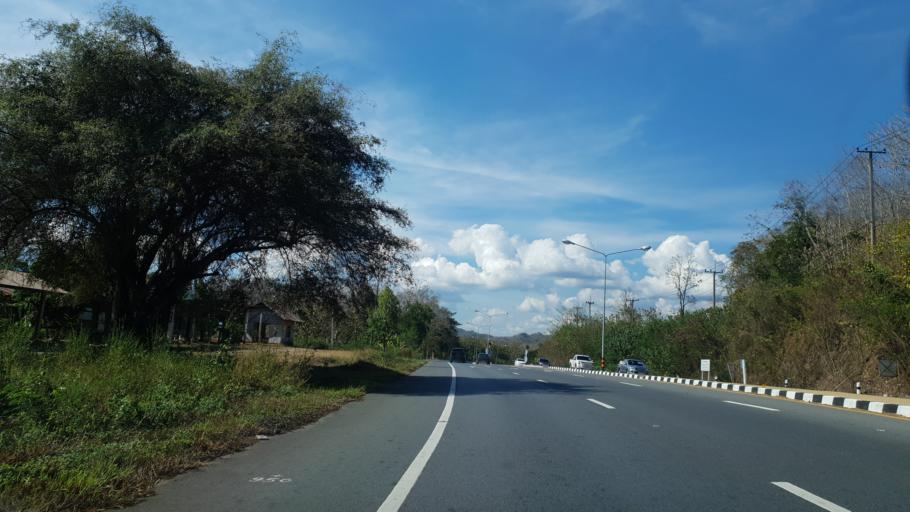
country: TH
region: Phrae
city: Den Chai
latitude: 17.9269
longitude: 100.0646
